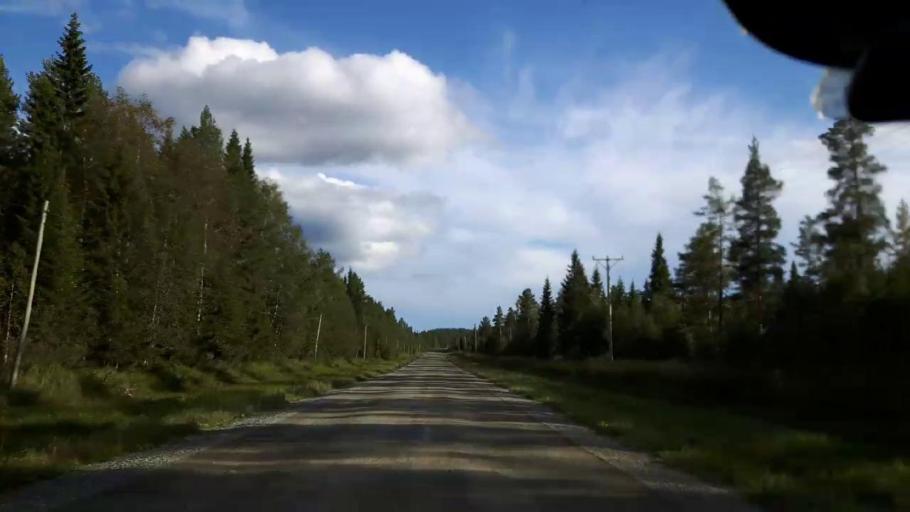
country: SE
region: Jaemtland
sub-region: Stroemsunds Kommun
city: Stroemsund
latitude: 63.3044
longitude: 15.5537
